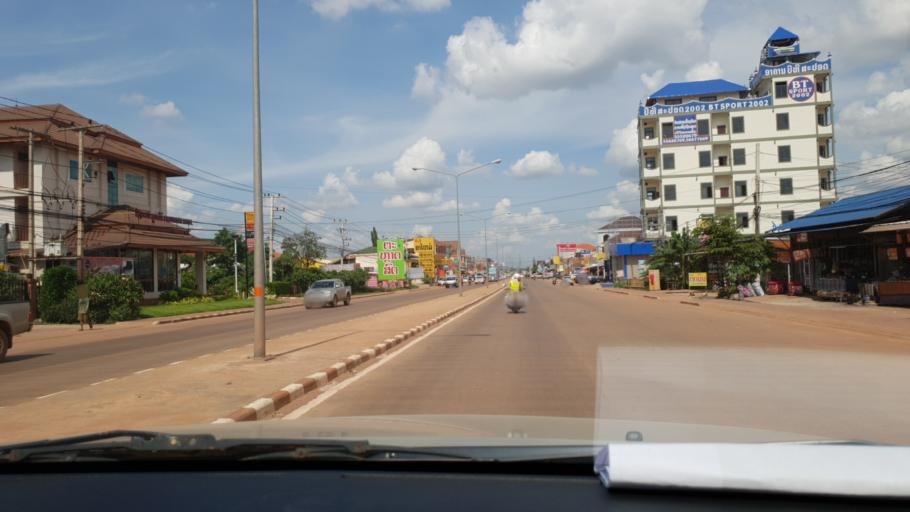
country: LA
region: Vientiane
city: Vientiane
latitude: 18.0325
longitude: 102.6419
